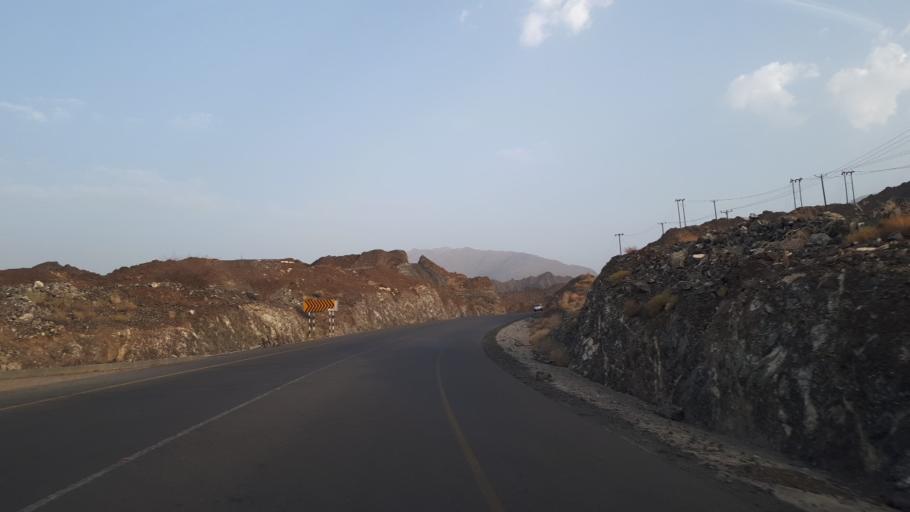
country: OM
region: Al Batinah
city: Rustaq
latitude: 23.4185
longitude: 57.3011
